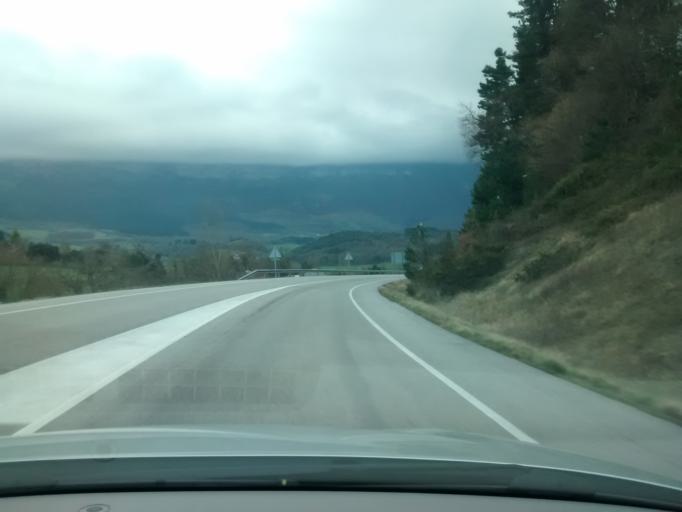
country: ES
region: Castille and Leon
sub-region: Provincia de Burgos
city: Villasana de Mena
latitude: 43.1003
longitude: -3.3063
